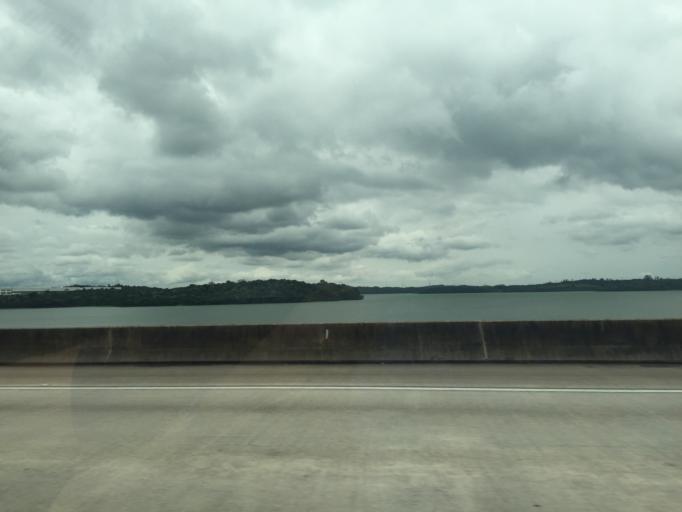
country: BR
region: Sao Paulo
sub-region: Diadema
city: Diadema
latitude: -23.7789
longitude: -46.6185
